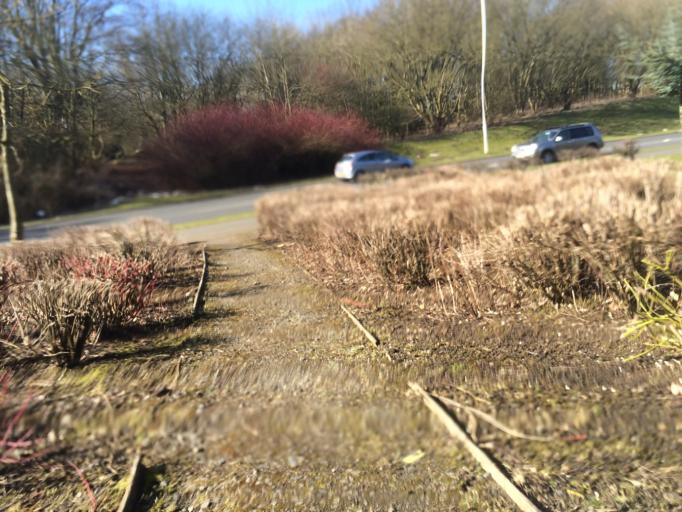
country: GB
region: Scotland
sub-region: Fife
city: Kirkcaldy
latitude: 56.1240
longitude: -3.2080
